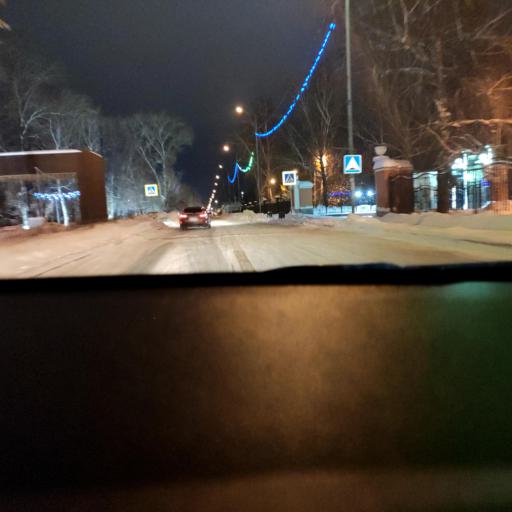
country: RU
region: Tatarstan
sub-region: Chistopol'skiy Rayon
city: Chistopol'
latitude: 55.3641
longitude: 50.6452
